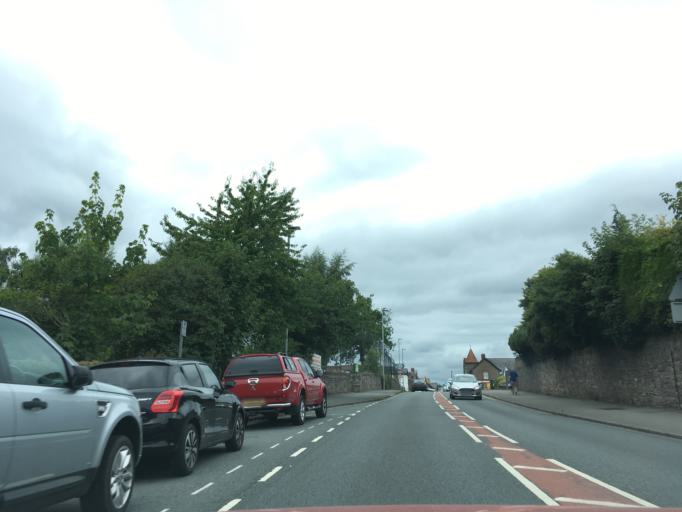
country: GB
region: Wales
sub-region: Monmouthshire
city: Gilwern
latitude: 51.8569
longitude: -3.1346
